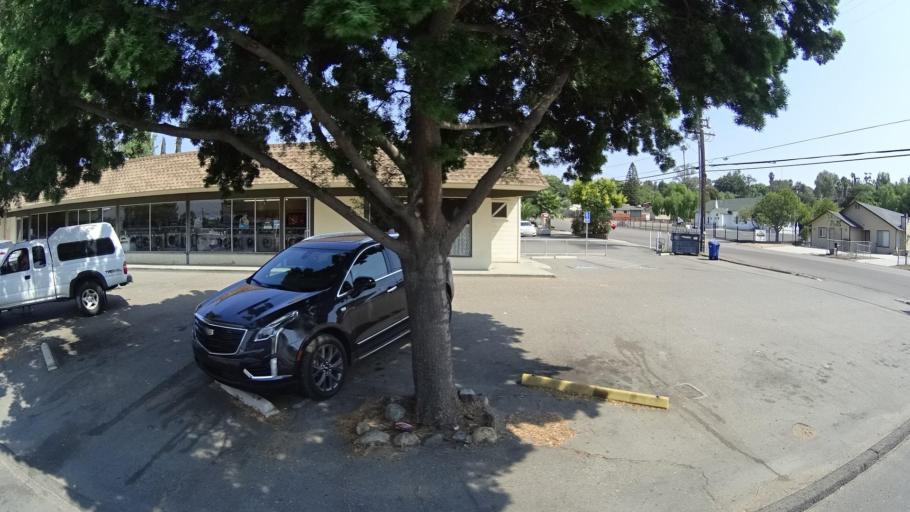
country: US
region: California
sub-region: San Diego County
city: Fallbrook
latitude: 33.3846
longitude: -117.2482
